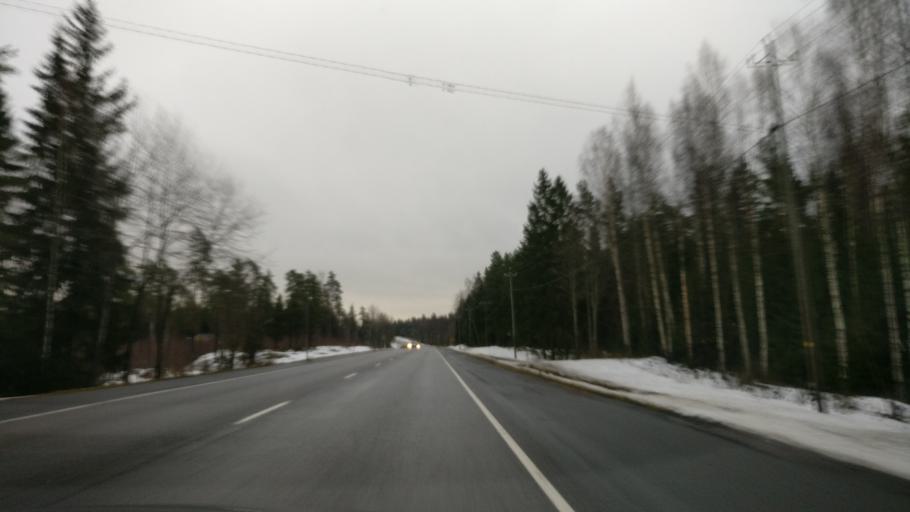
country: FI
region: Uusimaa
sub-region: Raaseporin
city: Inga
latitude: 60.0624
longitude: 23.8825
